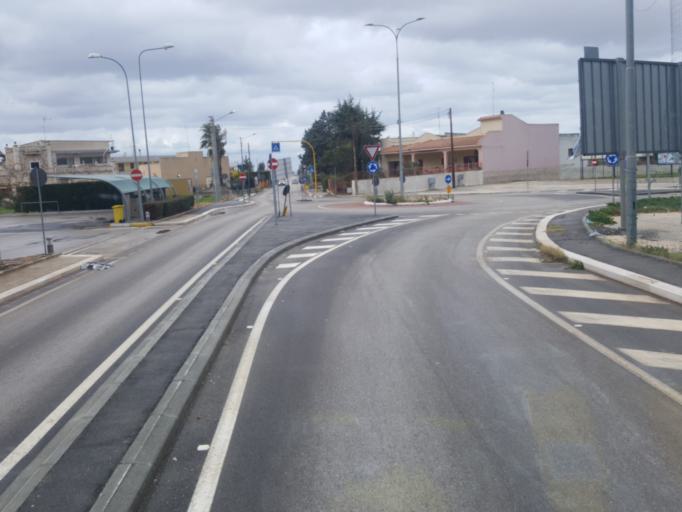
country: IT
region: Apulia
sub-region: Provincia di Bari
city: Turi
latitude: 40.9202
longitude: 17.0120
